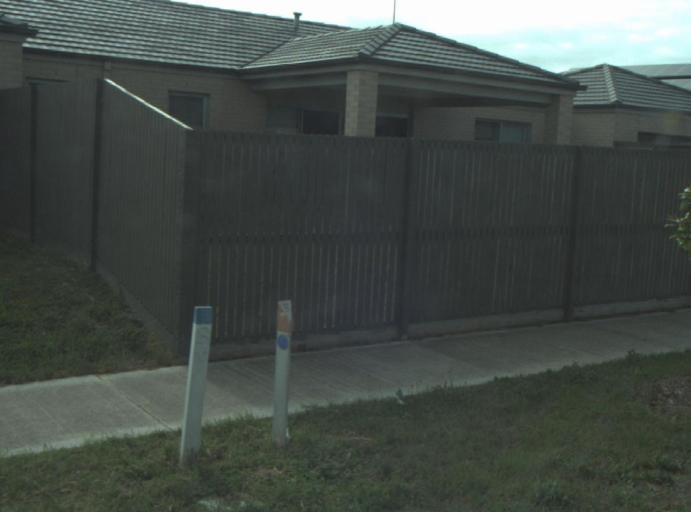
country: AU
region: Victoria
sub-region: Greater Geelong
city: Wandana Heights
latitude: -38.2090
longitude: 144.3151
